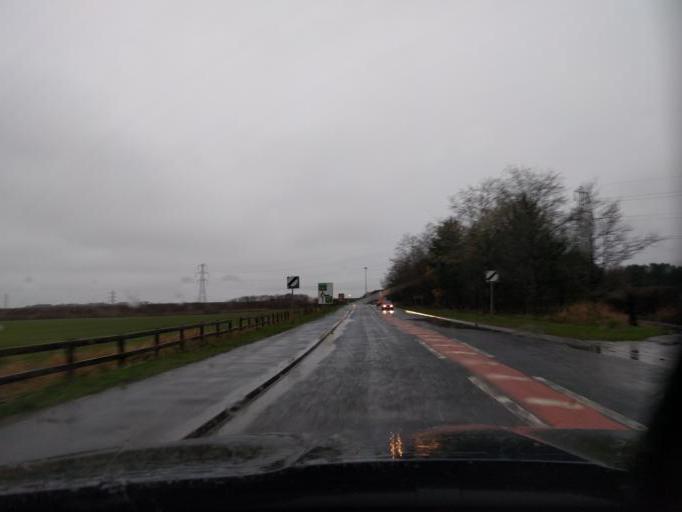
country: GB
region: England
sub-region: Northumberland
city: Newbiggin-by-the-Sea
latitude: 55.1924
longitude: -1.5351
